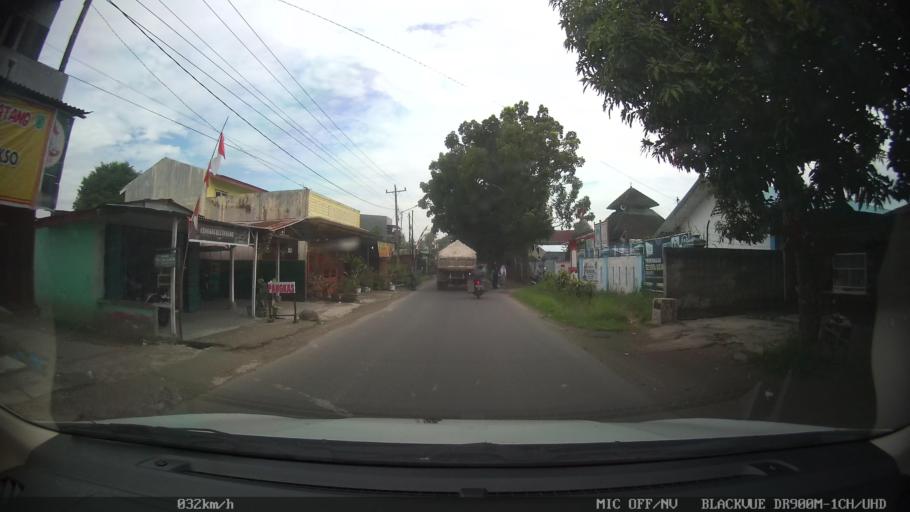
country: ID
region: North Sumatra
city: Sunggal
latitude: 3.6601
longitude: 98.5926
